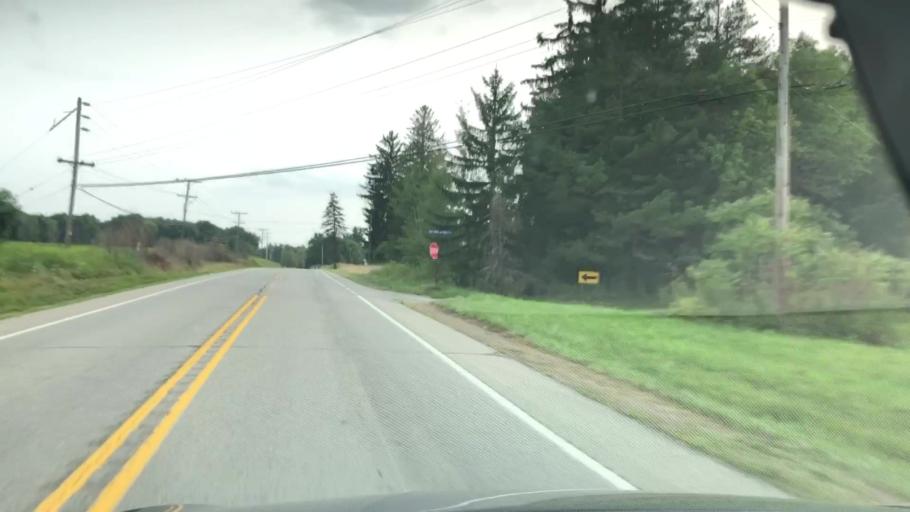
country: US
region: Pennsylvania
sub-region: Crawford County
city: Titusville
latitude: 41.5960
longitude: -79.6811
